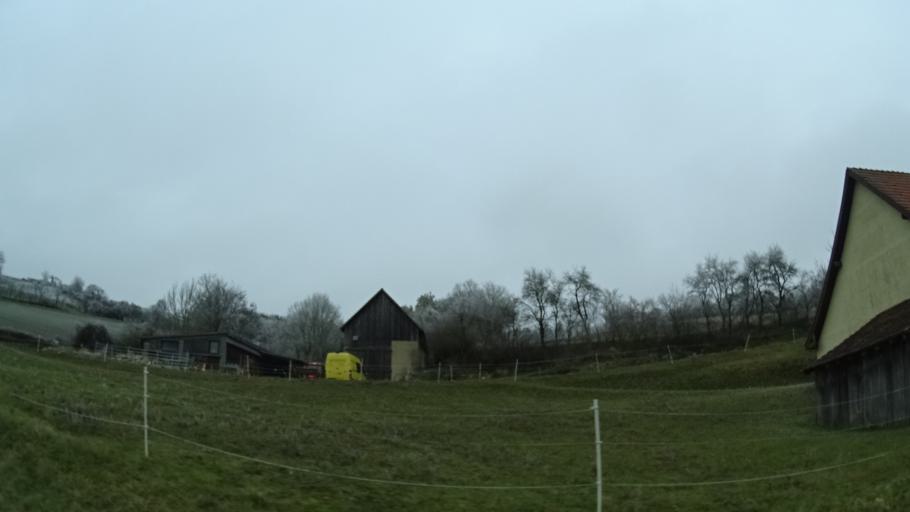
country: DE
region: Baden-Wuerttemberg
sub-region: Regierungsbezirk Stuttgart
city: Igersheim
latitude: 49.5407
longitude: 9.8018
